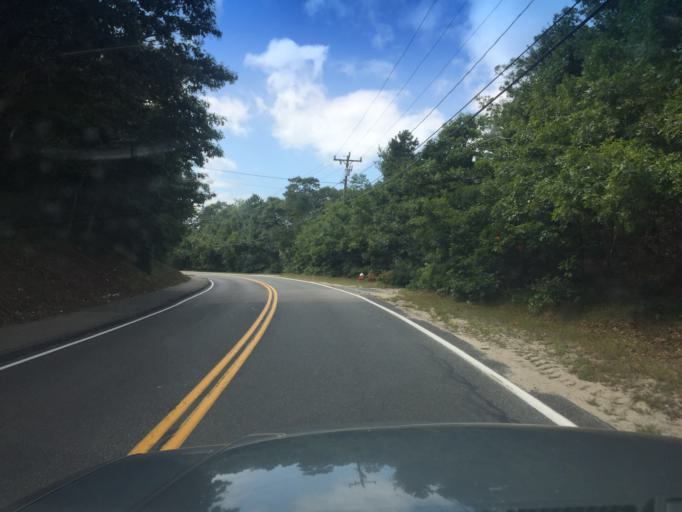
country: US
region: Massachusetts
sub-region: Barnstable County
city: Monument Beach
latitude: 41.7172
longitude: -70.5886
